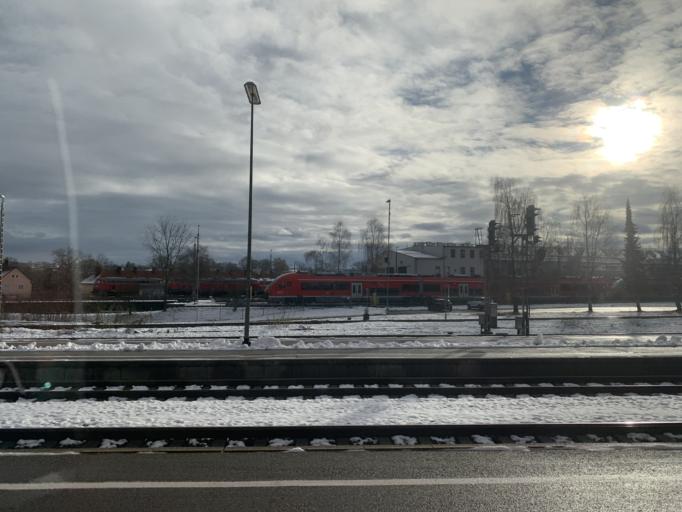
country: DE
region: Bavaria
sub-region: Swabia
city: Kempten (Allgaeu)
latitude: 47.7132
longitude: 10.3186
